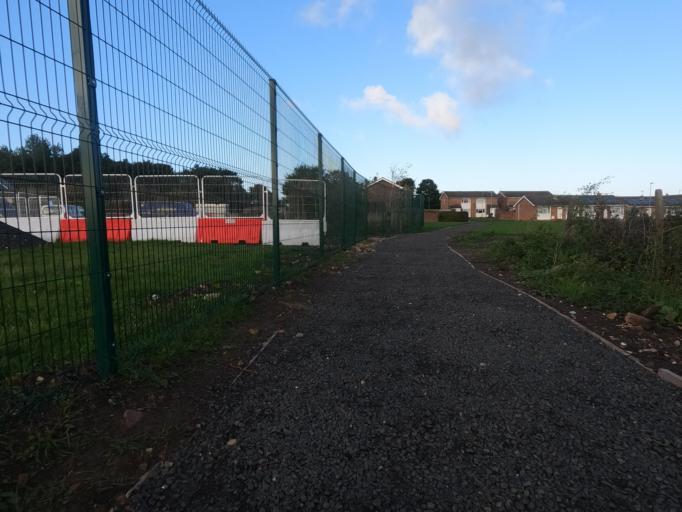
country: GB
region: England
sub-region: Northumberland
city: Seaton Delaval
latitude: 55.0745
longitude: -1.5364
